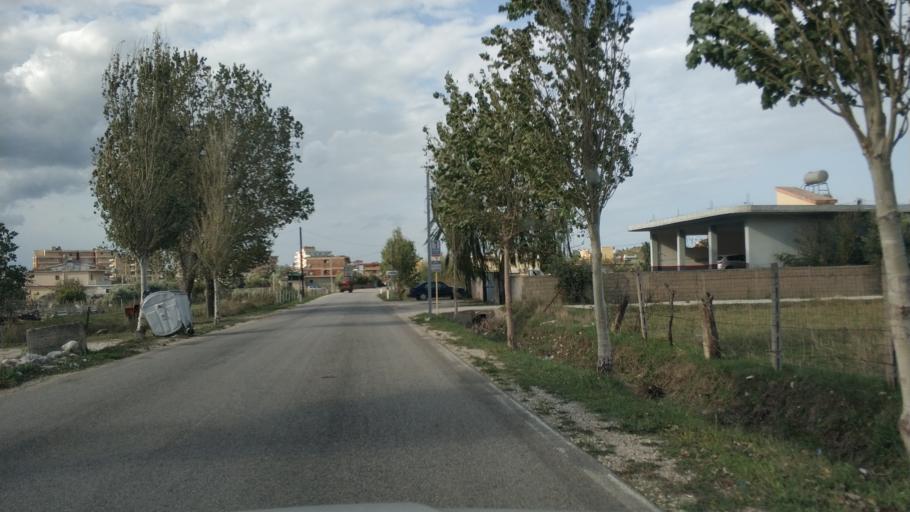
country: AL
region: Vlore
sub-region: Rrethi i Vlores
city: Orikum
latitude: 40.3253
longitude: 19.4795
